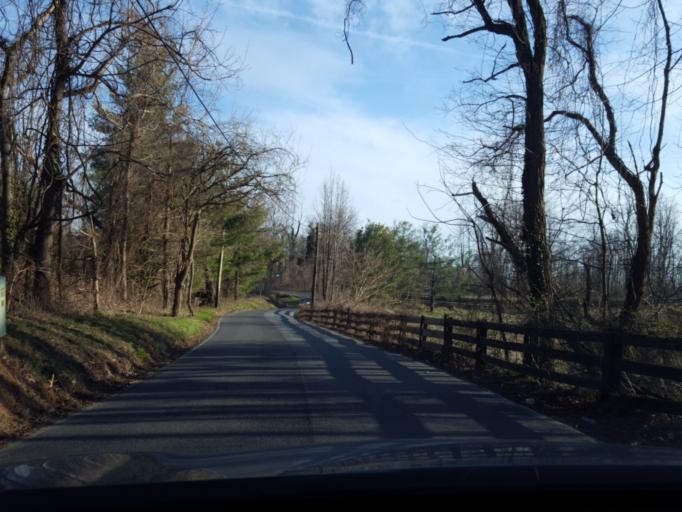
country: US
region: Maryland
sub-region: Anne Arundel County
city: Deale
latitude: 38.7556
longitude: -76.5791
